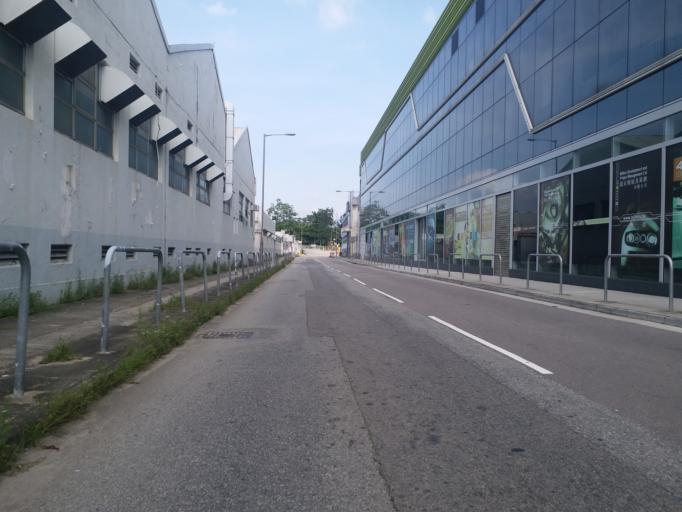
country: HK
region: Yuen Long
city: Yuen Long Kau Hui
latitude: 22.4442
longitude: 114.0036
